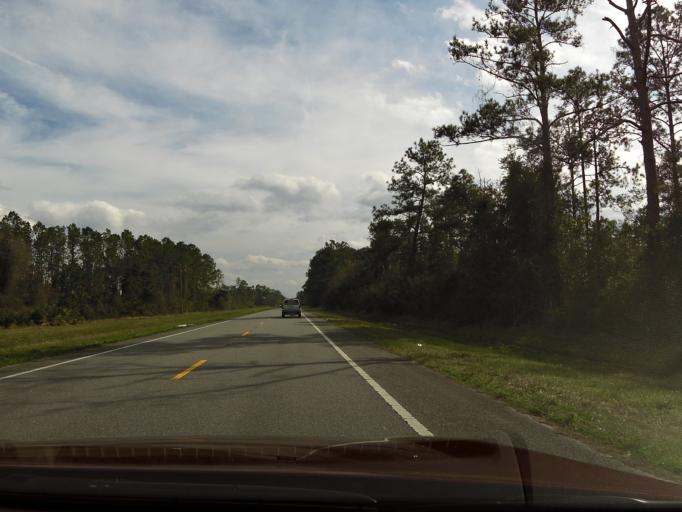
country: US
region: Florida
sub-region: Volusia County
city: De Leon Springs
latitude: 29.1924
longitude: -81.3113
